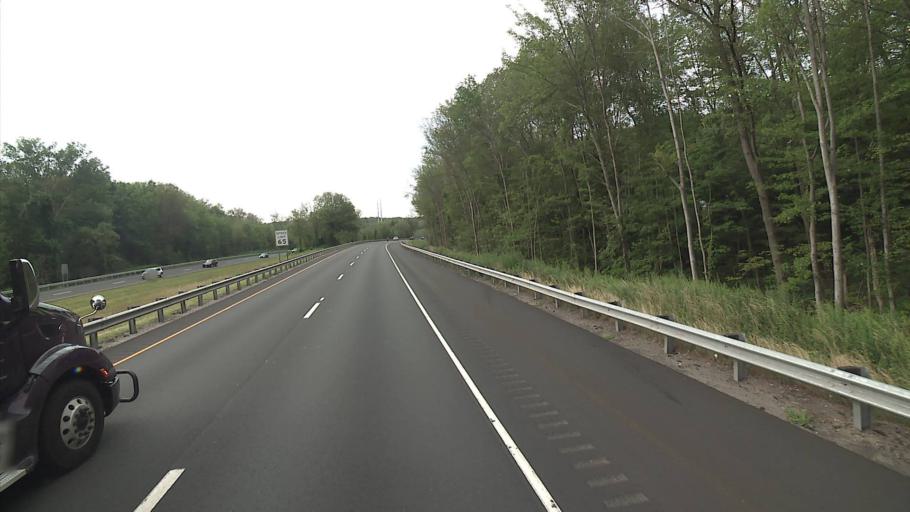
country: US
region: Connecticut
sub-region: New Haven County
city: Middlebury
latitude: 41.5288
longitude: -73.0885
